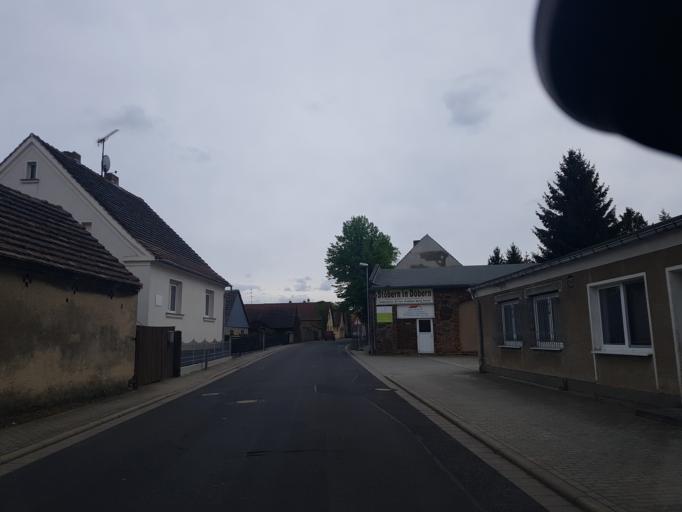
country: DE
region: Brandenburg
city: Tschernitz
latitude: 51.6214
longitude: 14.6012
